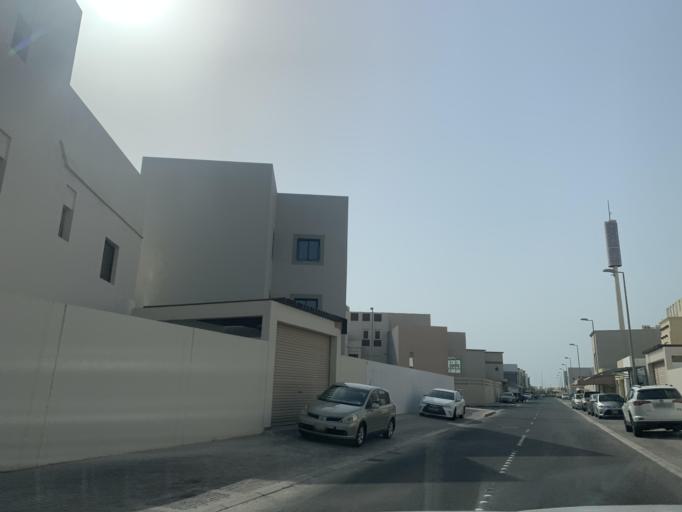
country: BH
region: Manama
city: Jidd Hafs
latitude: 26.2235
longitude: 50.4499
